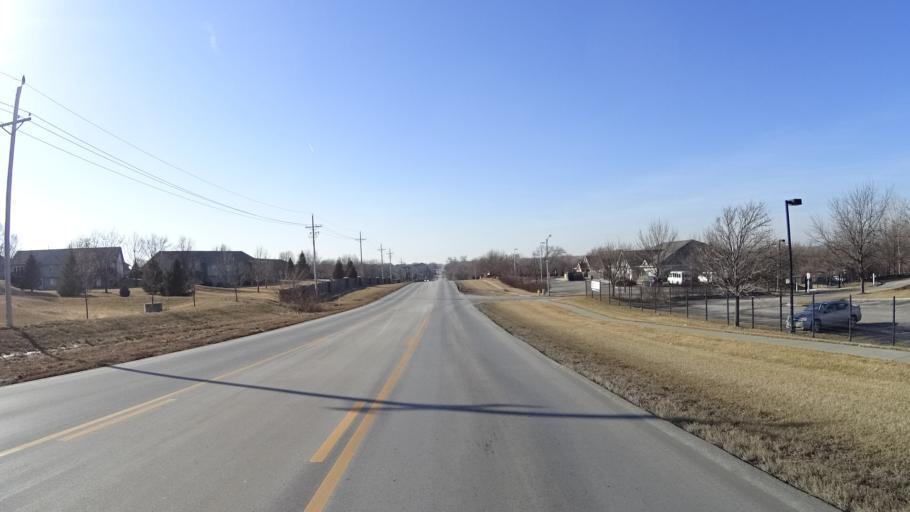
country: US
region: Nebraska
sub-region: Douglas County
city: Bennington
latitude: 41.3067
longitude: -96.1212
